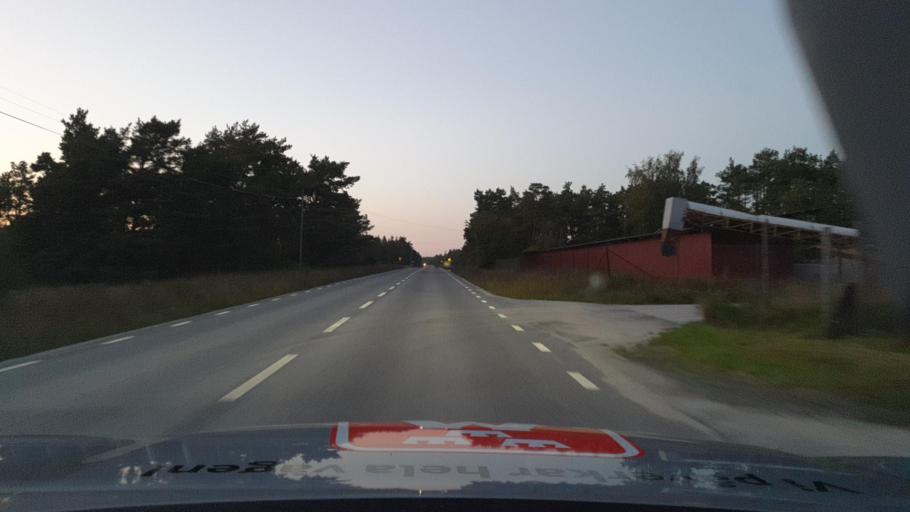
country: SE
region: Gotland
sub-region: Gotland
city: Slite
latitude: 57.7251
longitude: 18.7888
